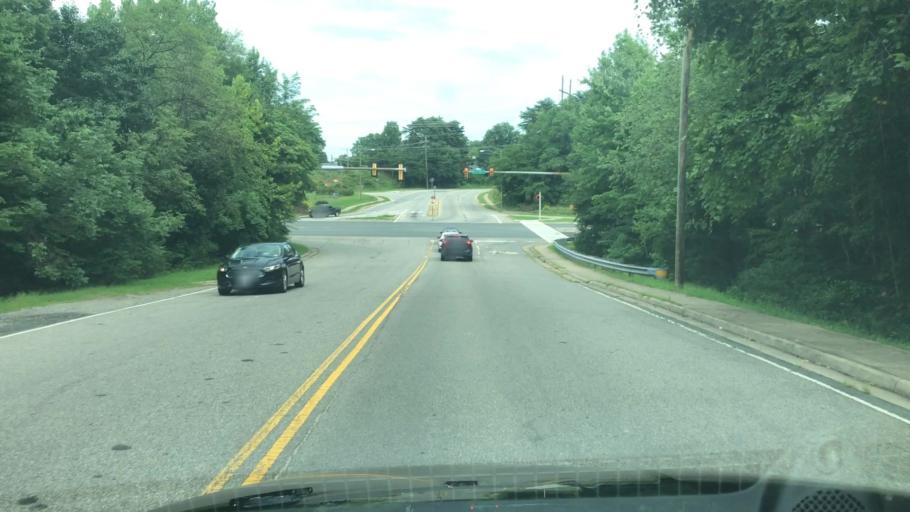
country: US
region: Virginia
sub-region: City of Fredericksburg
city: Fredericksburg
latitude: 38.2941
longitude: -77.4817
